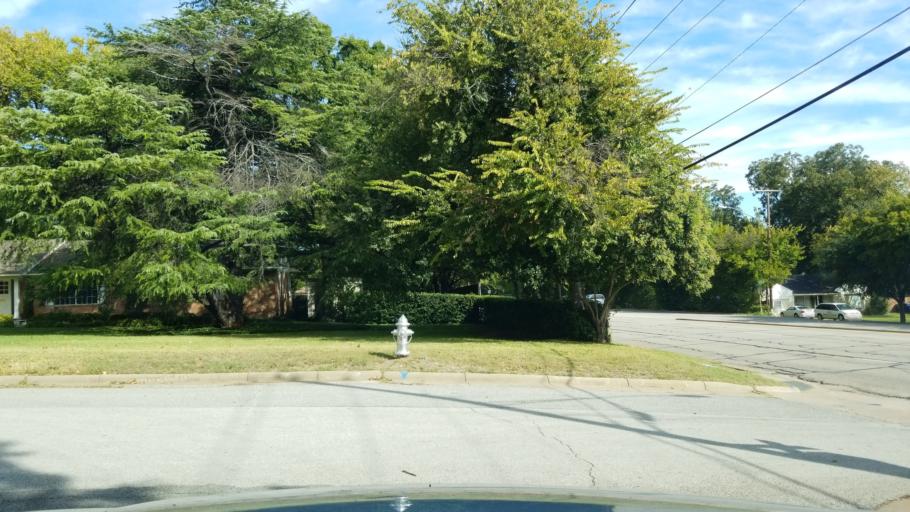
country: US
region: Texas
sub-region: Dallas County
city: Garland
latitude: 32.9000
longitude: -96.6489
